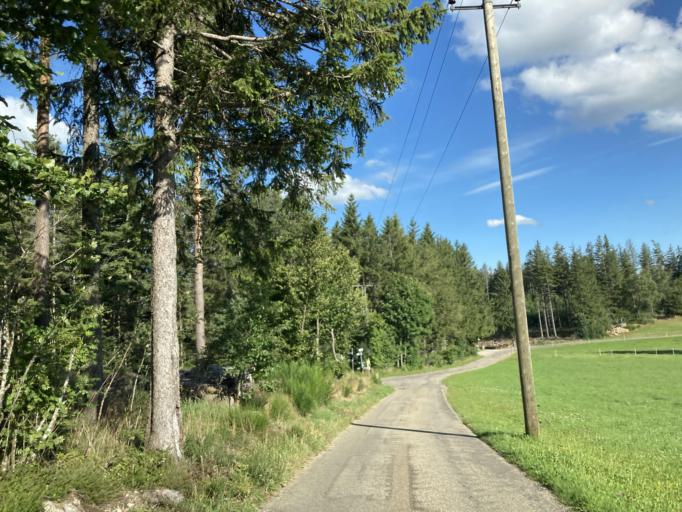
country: DE
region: Baden-Wuerttemberg
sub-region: Freiburg Region
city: Schonach im Schwarzwald
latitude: 48.1478
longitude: 8.2114
